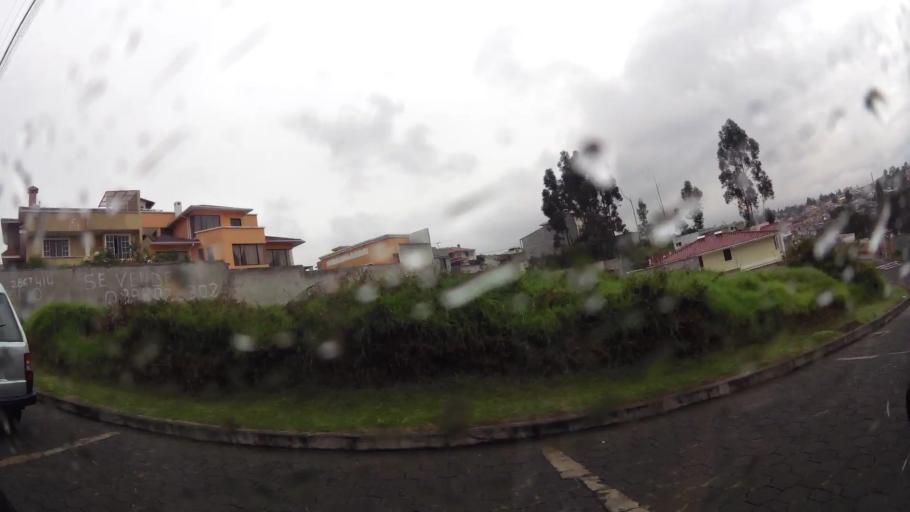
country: EC
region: Pichincha
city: Sangolqui
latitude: -0.3200
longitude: -78.4373
